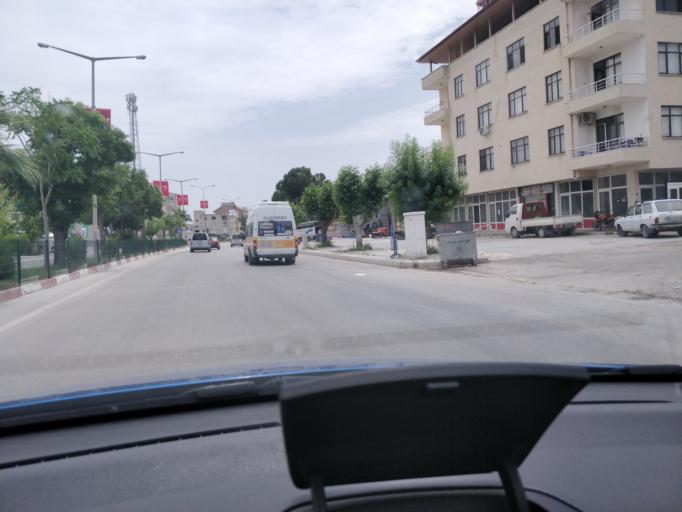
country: TR
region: Mersin
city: Mut
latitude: 36.6364
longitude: 33.4458
